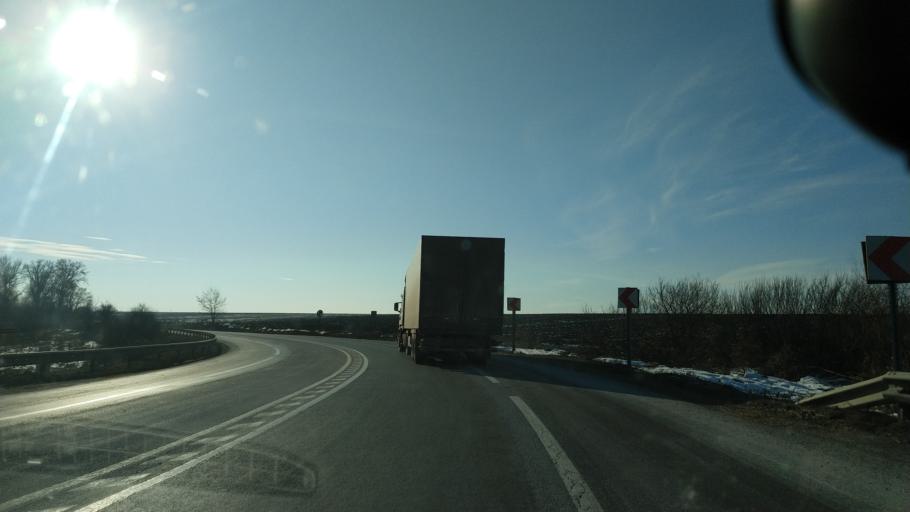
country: RO
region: Iasi
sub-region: Comuna Butea
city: Butea
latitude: 47.1028
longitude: 26.9223
